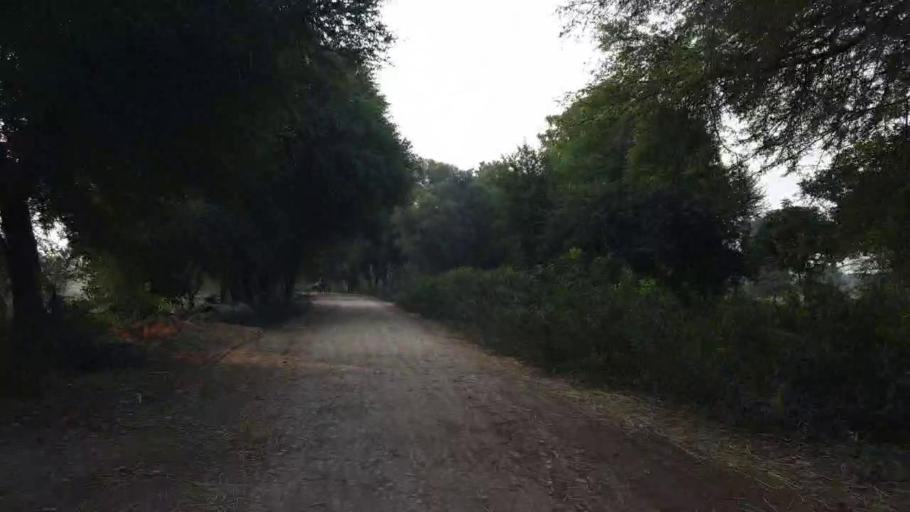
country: PK
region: Sindh
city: Tando Muhammad Khan
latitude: 25.1770
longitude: 68.6032
